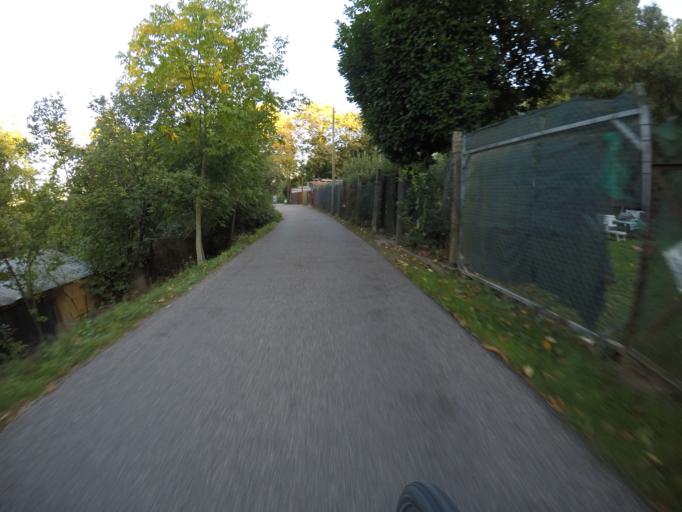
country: DE
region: Baden-Wuerttemberg
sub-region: Regierungsbezirk Stuttgart
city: Stuttgart-Ost
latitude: 48.7800
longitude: 9.2263
